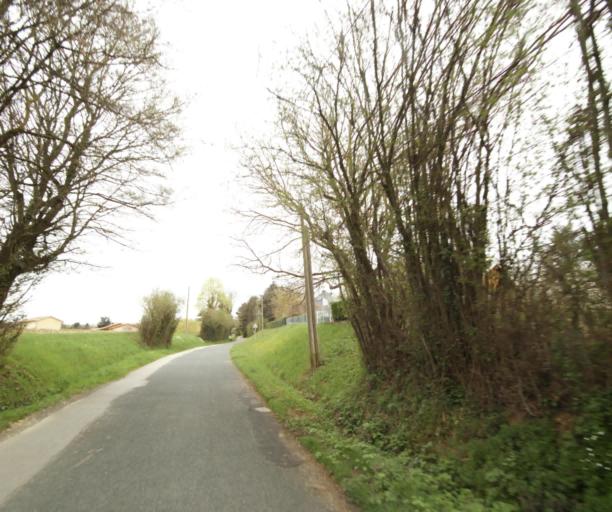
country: FR
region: Bourgogne
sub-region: Departement de Saone-et-Loire
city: Charnay-les-Macon
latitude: 46.3168
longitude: 4.8052
